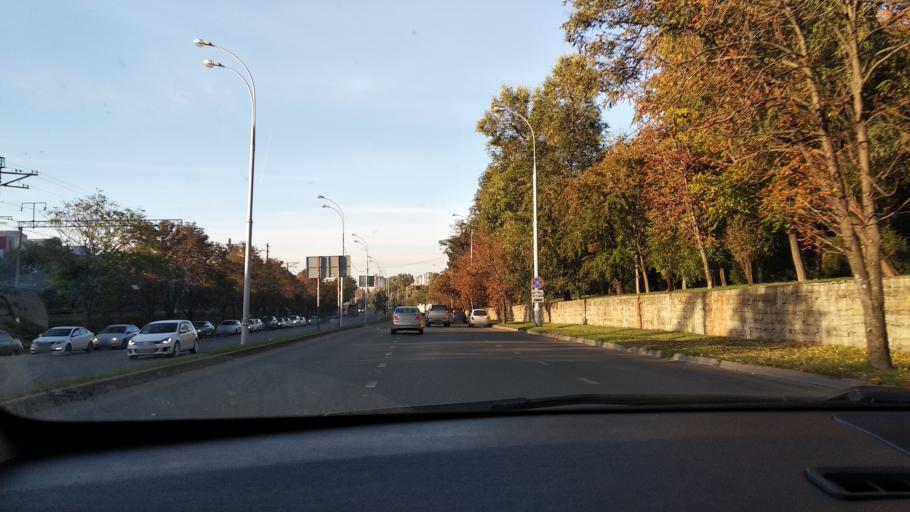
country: RU
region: Krasnodarskiy
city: Krasnodar
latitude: 45.0116
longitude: 38.9729
